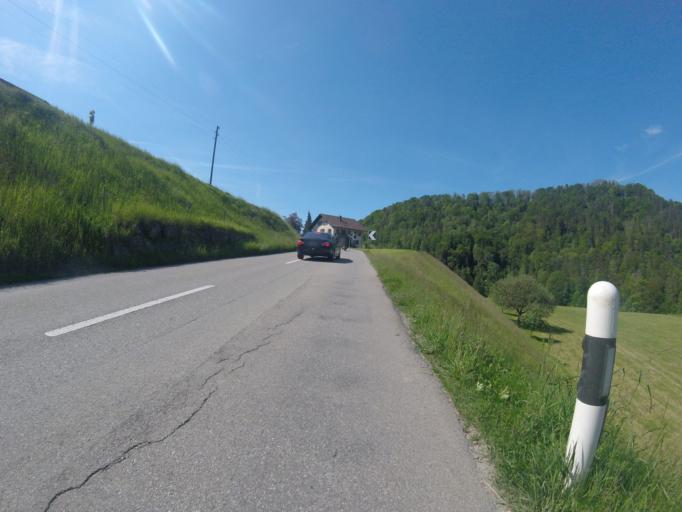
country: CH
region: Saint Gallen
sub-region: Wahlkreis Toggenburg
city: Ganterschwil
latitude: 47.3805
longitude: 9.1124
